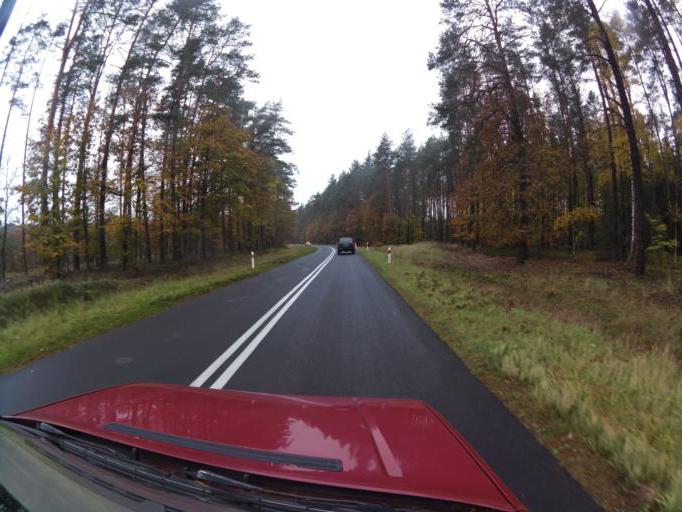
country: PL
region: West Pomeranian Voivodeship
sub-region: Powiat policki
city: Dobra
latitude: 53.5822
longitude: 14.4195
